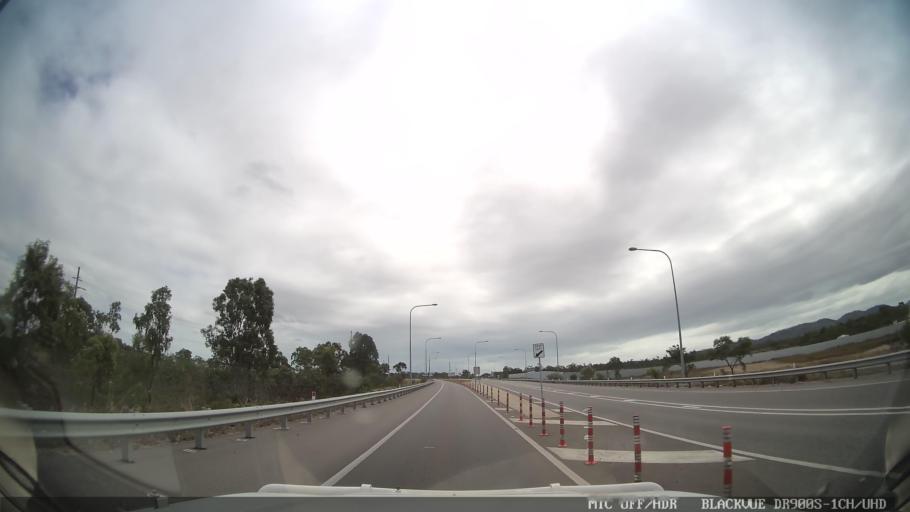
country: AU
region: Queensland
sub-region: Townsville
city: Bohle Plains
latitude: -19.3039
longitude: 146.6957
